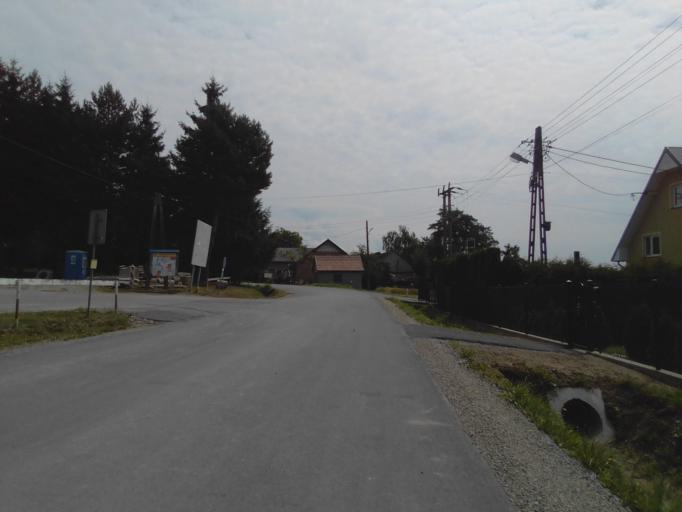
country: PL
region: Subcarpathian Voivodeship
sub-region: Powiat jasielski
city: Tarnowiec
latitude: 49.7713
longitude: 21.5706
